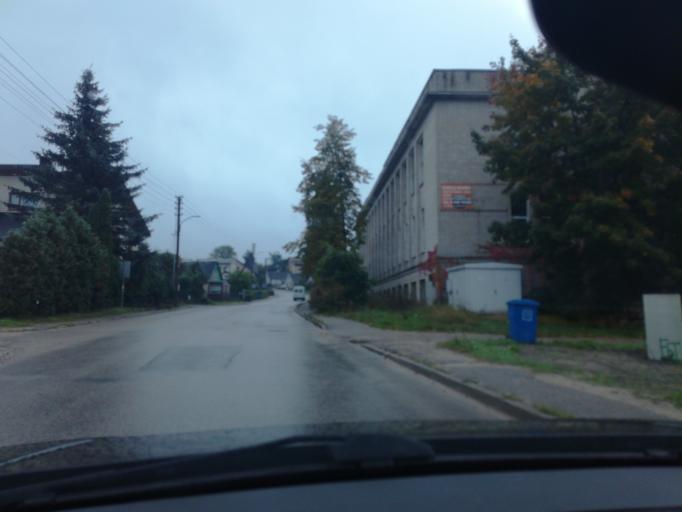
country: LT
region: Alytaus apskritis
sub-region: Alytus
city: Alytus
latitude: 54.4016
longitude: 24.0686
